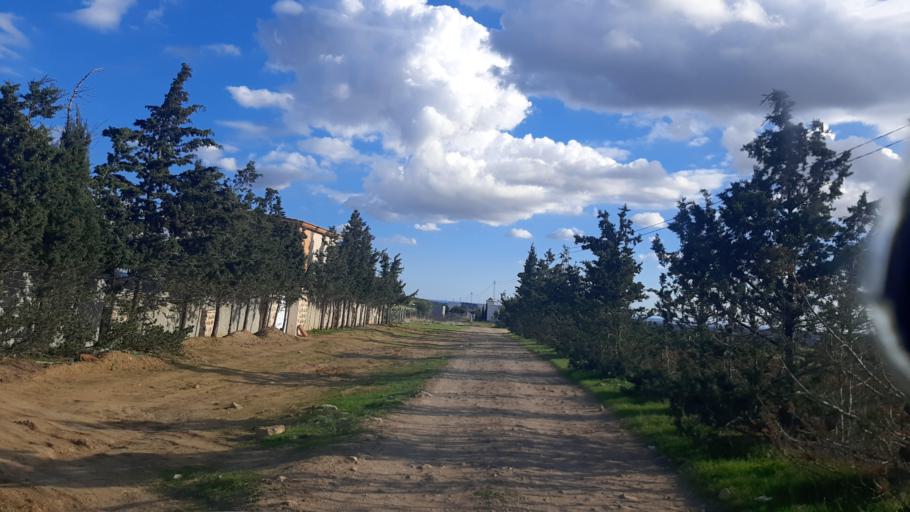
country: TN
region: Nabul
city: Bu `Urqub
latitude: 36.4682
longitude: 10.4789
